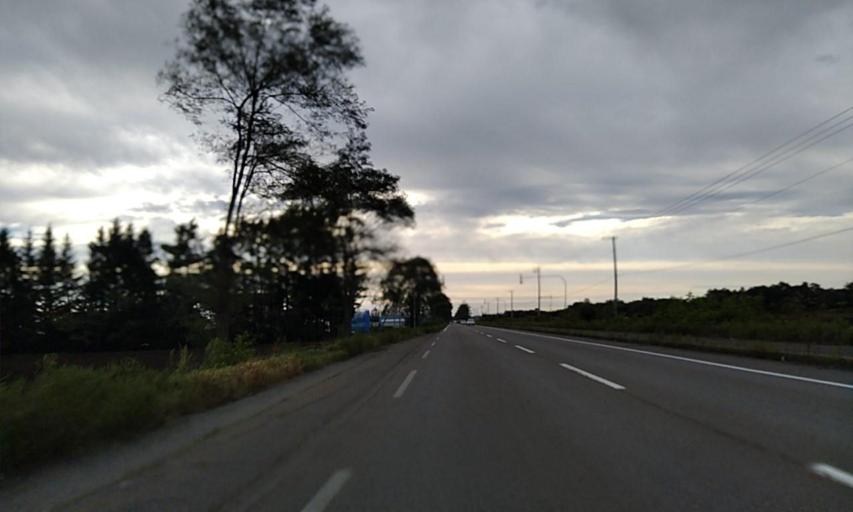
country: JP
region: Hokkaido
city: Obihiro
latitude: 42.9298
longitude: 142.9805
